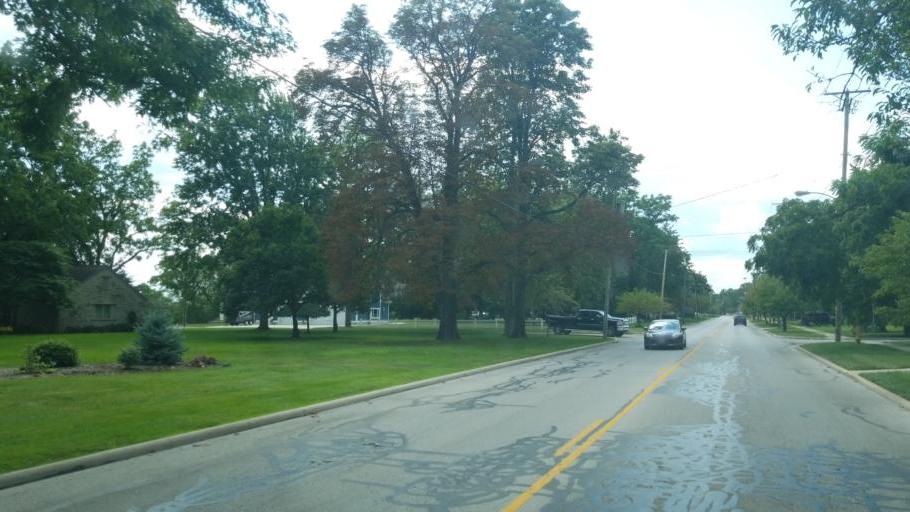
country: US
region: Ohio
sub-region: Wood County
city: Perrysburg
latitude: 41.5731
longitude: -83.6318
